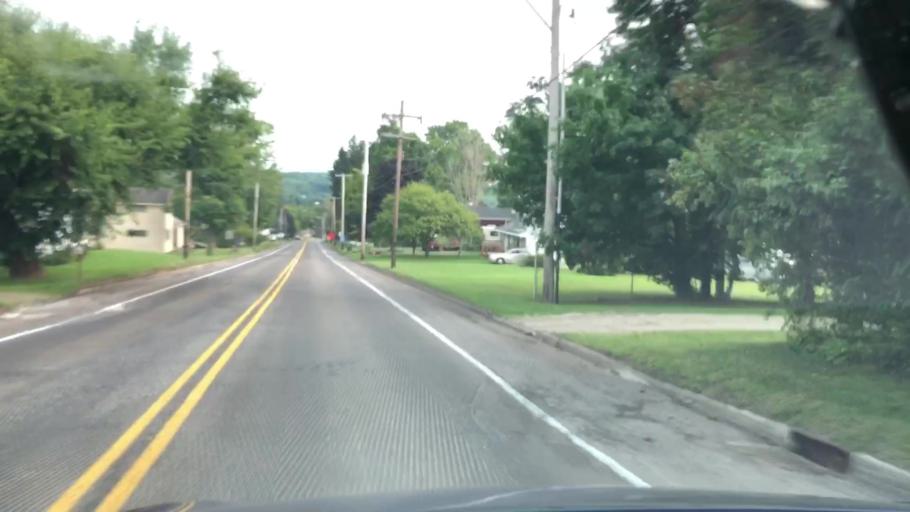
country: US
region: Pennsylvania
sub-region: Crawford County
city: Titusville
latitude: 41.7410
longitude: -79.7650
